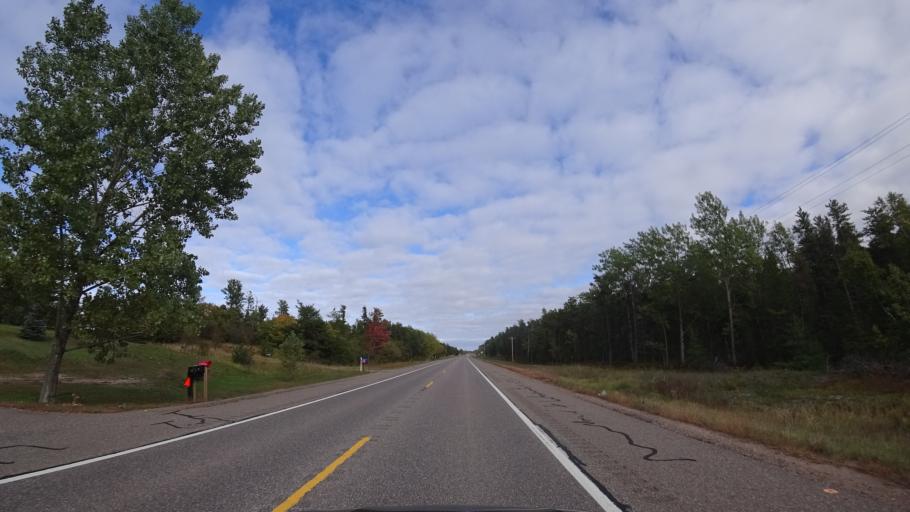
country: US
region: Michigan
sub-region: Marquette County
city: Harvey
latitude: 46.4901
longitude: -87.2013
